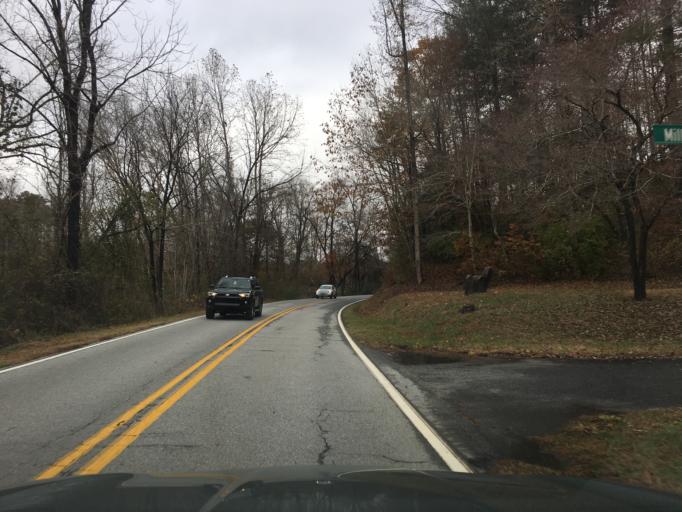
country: US
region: North Carolina
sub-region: Rutherford County
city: Rutherfordton
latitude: 35.3177
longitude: -81.9801
